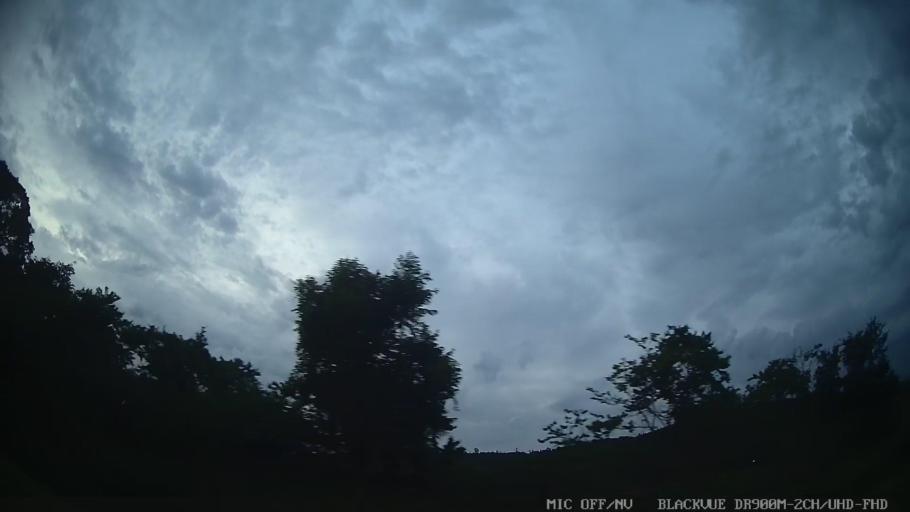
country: BR
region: Sao Paulo
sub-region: Amparo
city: Amparo
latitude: -22.8153
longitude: -46.7555
